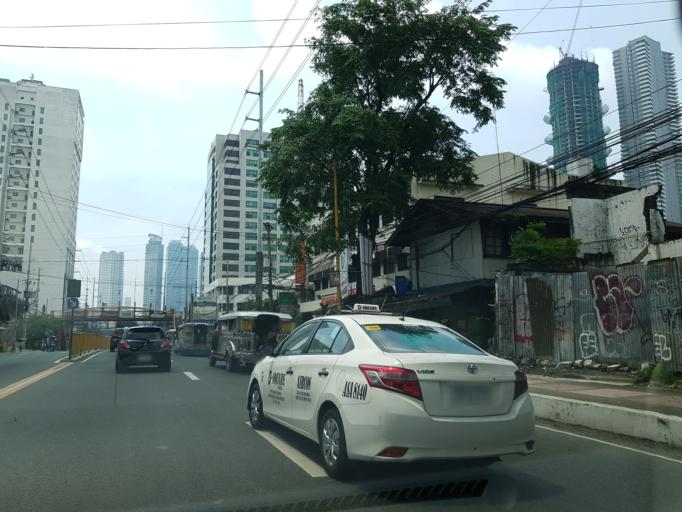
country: PH
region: Metro Manila
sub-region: Pasig
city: Pasig City
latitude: 14.5721
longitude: 121.0645
